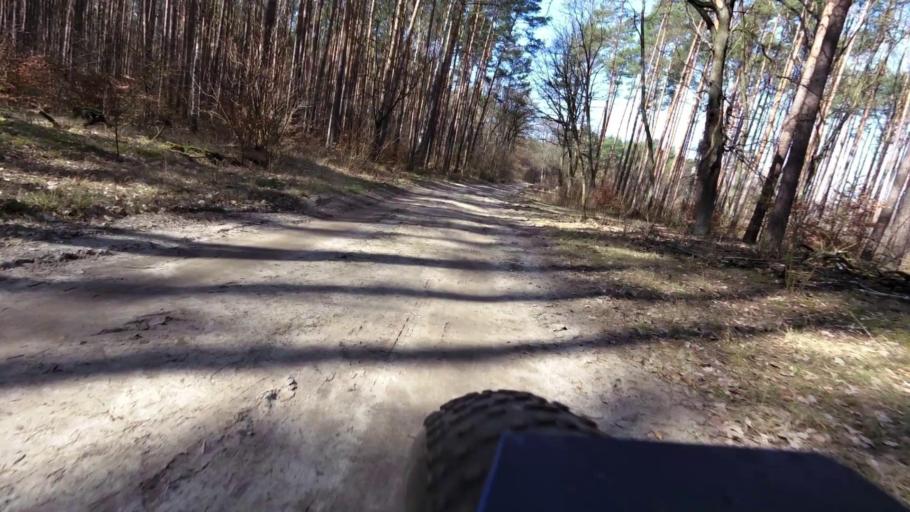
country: PL
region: Lubusz
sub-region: Powiat slubicki
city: Cybinka
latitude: 52.2040
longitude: 14.8761
